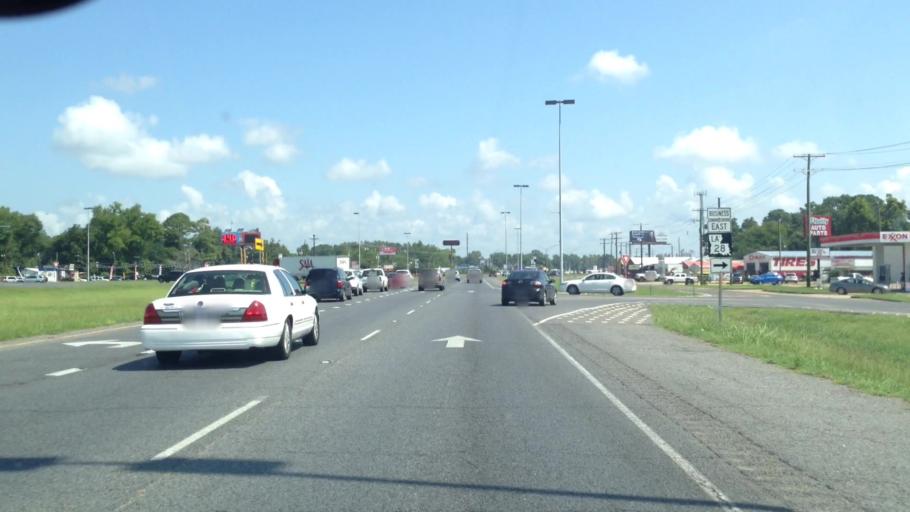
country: US
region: Louisiana
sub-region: Rapides Parish
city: Alexandria
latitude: 31.2995
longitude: -92.4796
